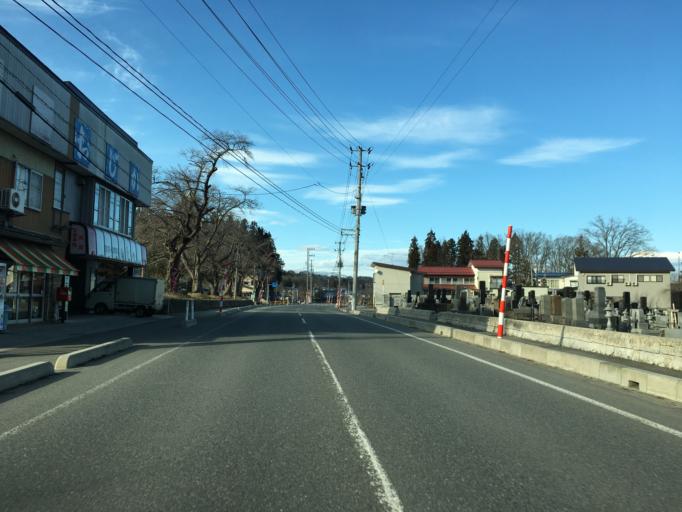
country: JP
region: Yamagata
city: Nagai
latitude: 38.0051
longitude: 139.9602
